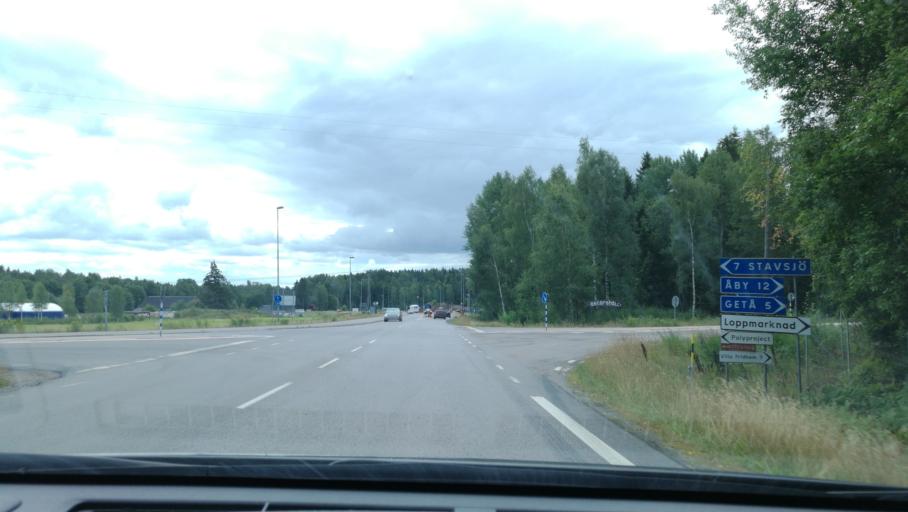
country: SE
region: OEstergoetland
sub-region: Norrkopings Kommun
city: Krokek
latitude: 58.6885
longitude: 16.3412
